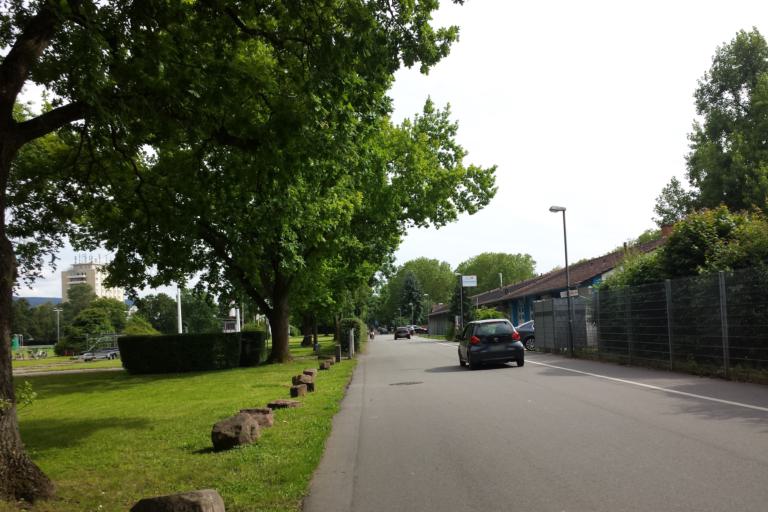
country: DE
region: Baden-Wuerttemberg
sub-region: Karlsruhe Region
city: Eppelheim
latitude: 49.4221
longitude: 8.6585
